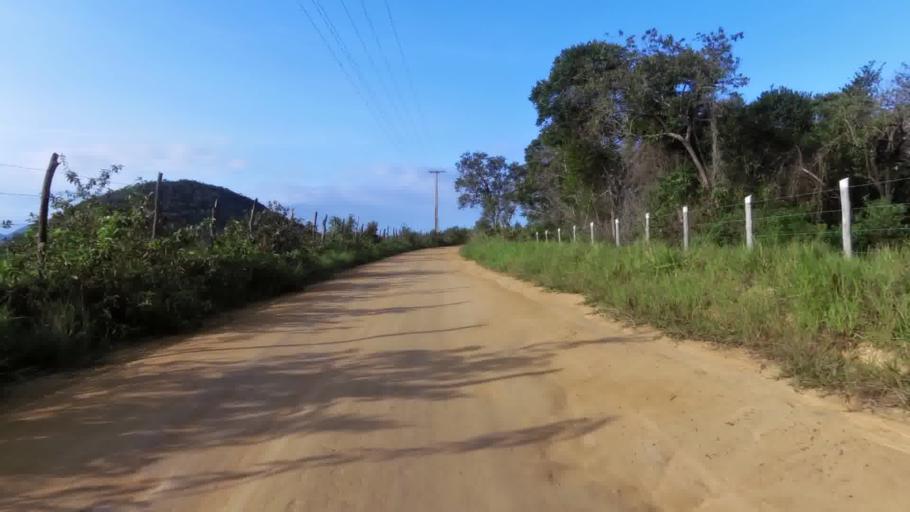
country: BR
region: Espirito Santo
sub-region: Guarapari
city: Guarapari
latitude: -20.7253
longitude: -40.5761
